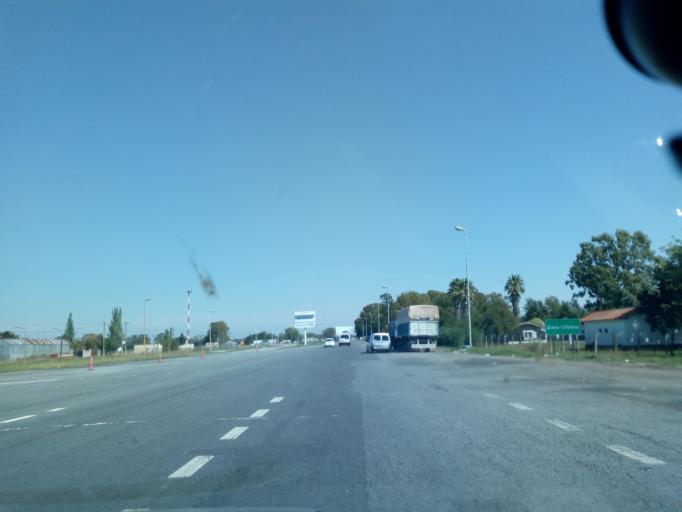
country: AR
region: Buenos Aires
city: Maipu
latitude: -36.8472
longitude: -57.8675
